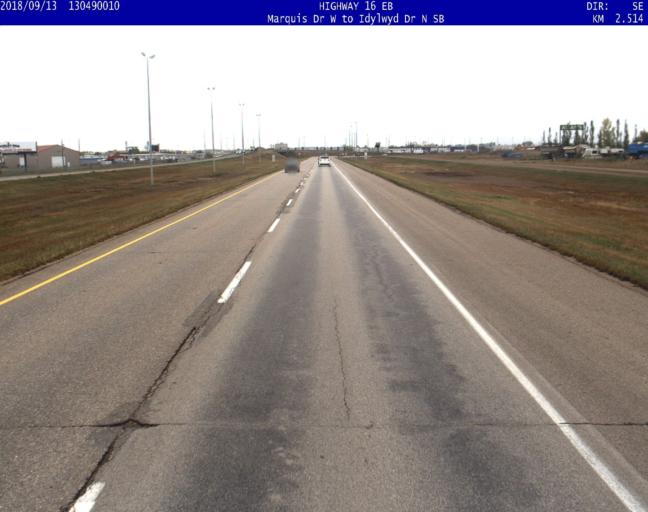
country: CA
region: Saskatchewan
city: Saskatoon
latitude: 52.1863
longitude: -106.6787
